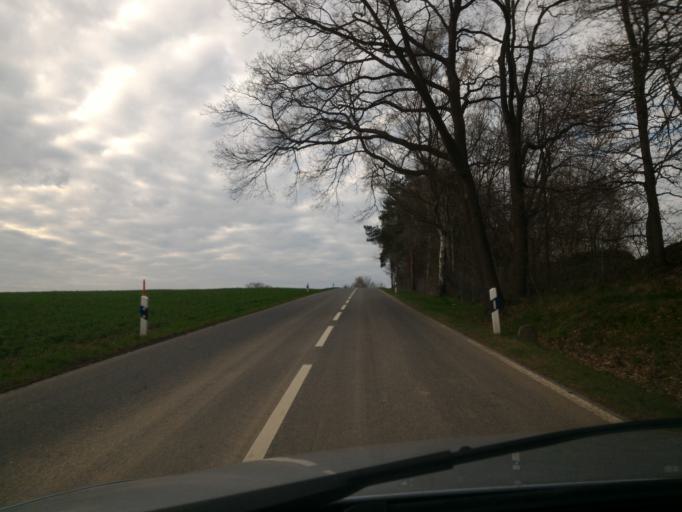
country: DE
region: Saxony
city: Hainewalde
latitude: 50.9234
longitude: 14.7019
